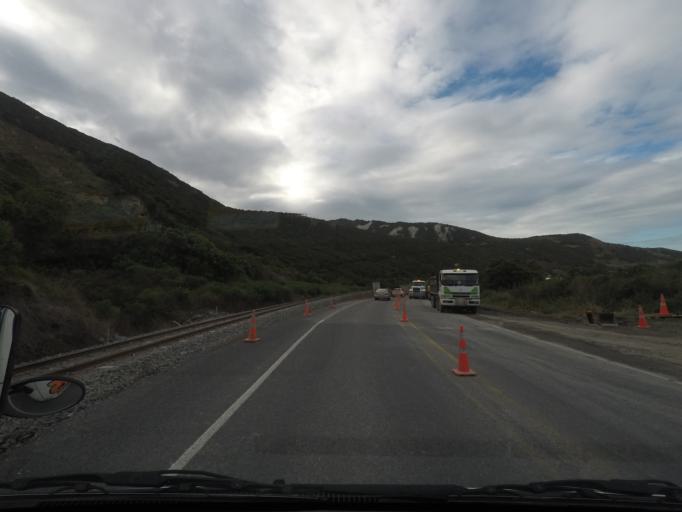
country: NZ
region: Canterbury
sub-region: Kaikoura District
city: Kaikoura
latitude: -42.2187
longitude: 173.8576
